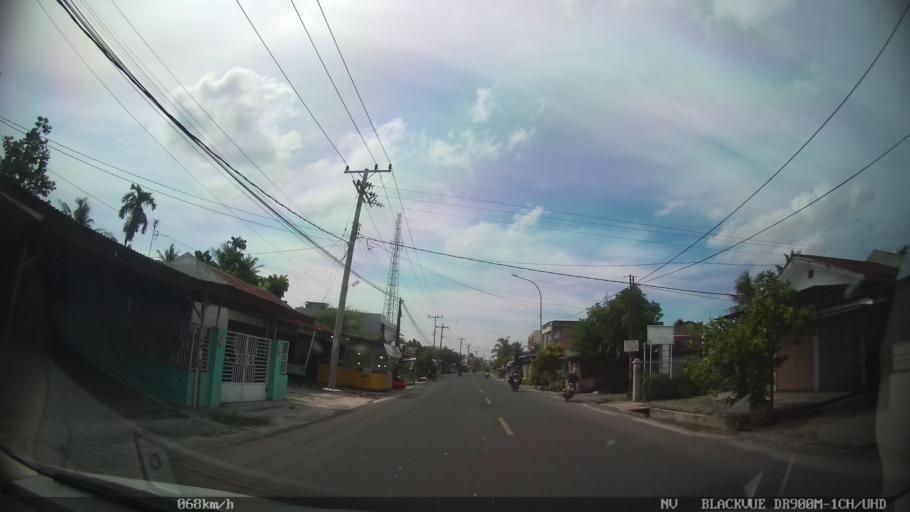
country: ID
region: North Sumatra
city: Percut
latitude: 3.5809
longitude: 98.8632
